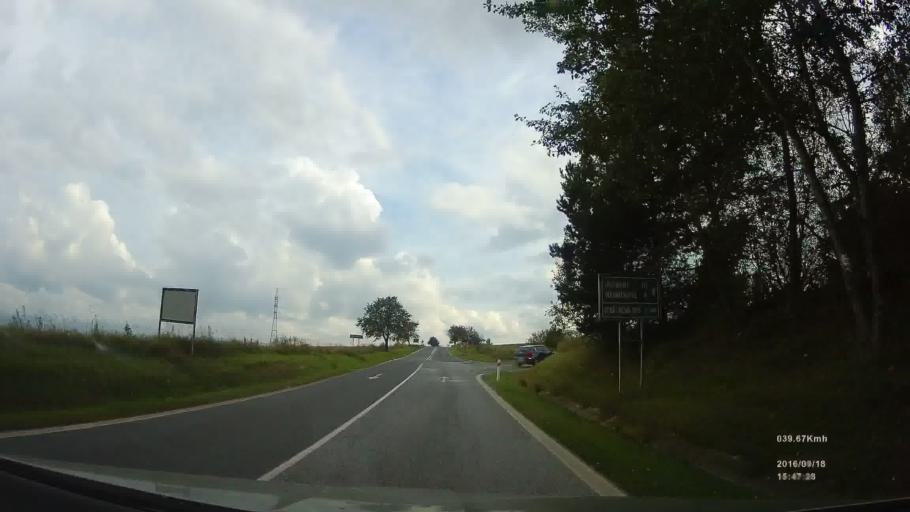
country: SK
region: Kosicky
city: Spisska Nova Ves
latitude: 48.9372
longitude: 20.5902
